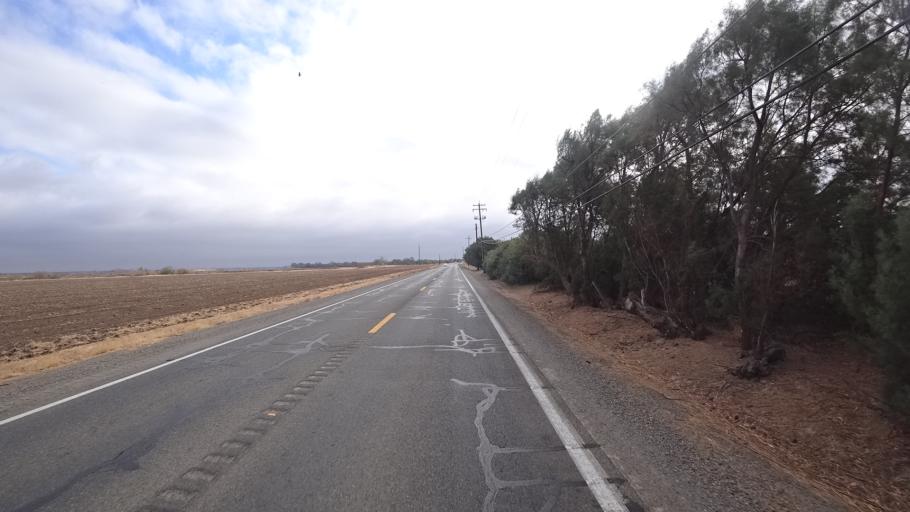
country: US
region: California
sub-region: Yolo County
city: Esparto
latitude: 38.7062
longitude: -122.0419
